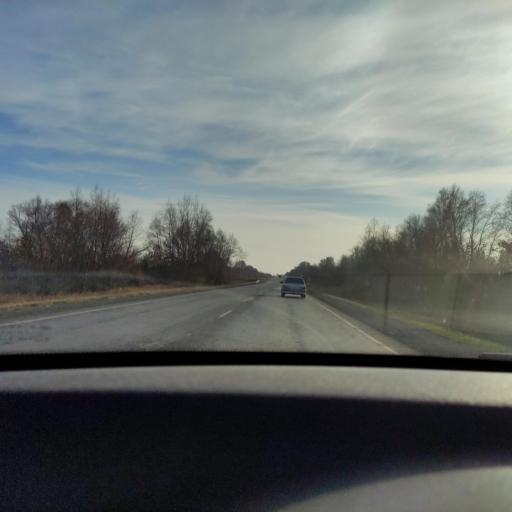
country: RU
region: Samara
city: Krasnoarmeyskoye
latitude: 52.7636
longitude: 50.0259
